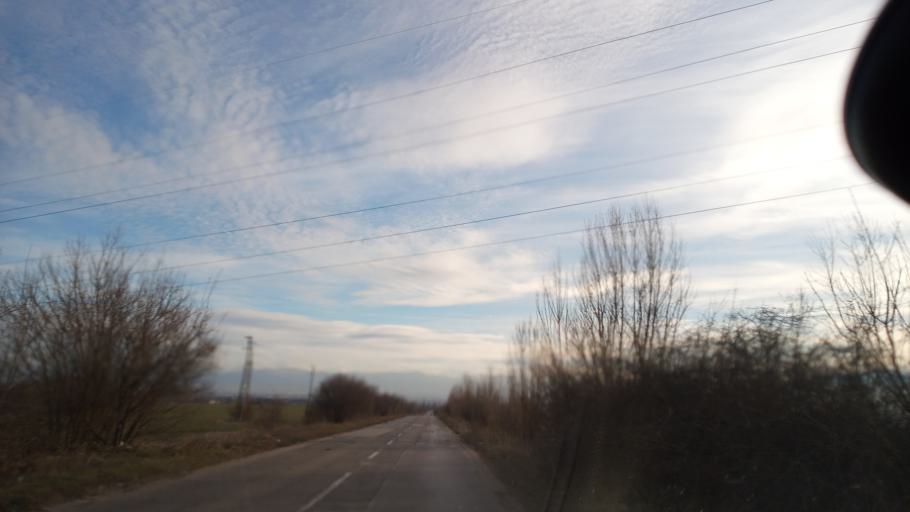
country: BG
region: Sofia-Capital
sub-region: Stolichna Obshtina
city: Bukhovo
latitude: 42.7540
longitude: 23.5582
